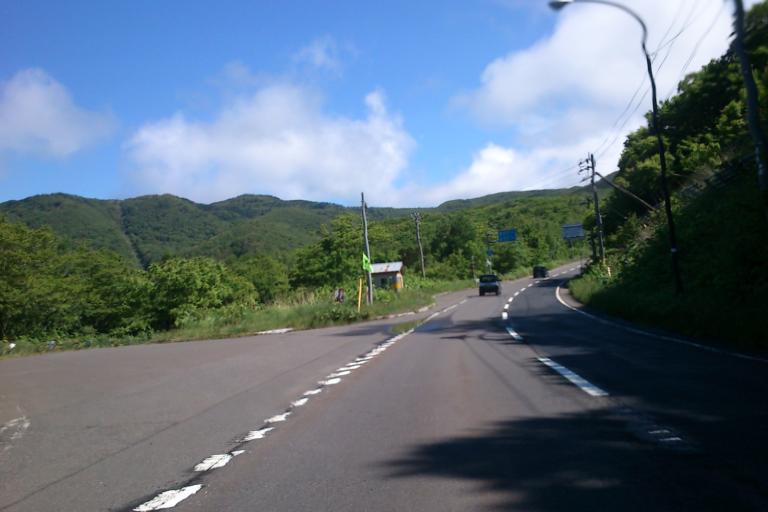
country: JP
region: Hokkaido
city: Ishikari
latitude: 43.5069
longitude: 141.3737
